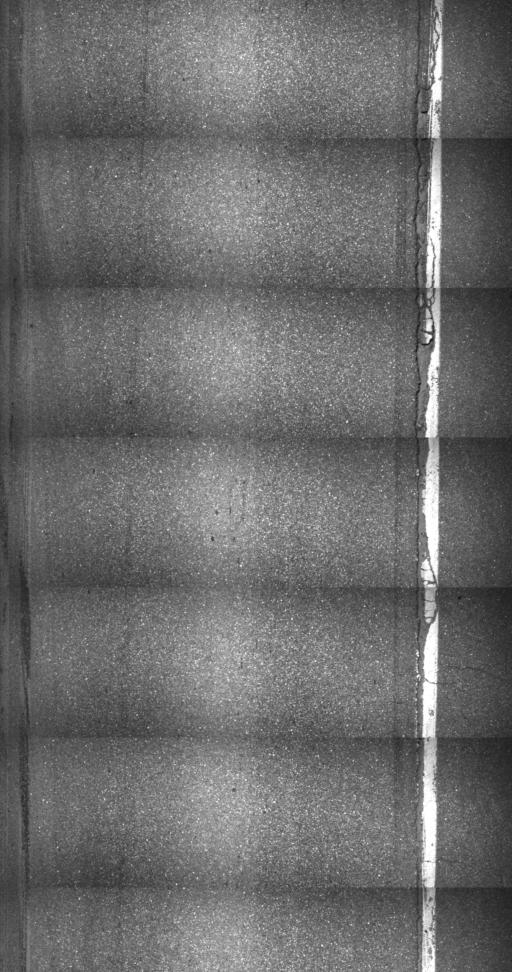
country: US
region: Vermont
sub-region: Chittenden County
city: Jericho
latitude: 44.6248
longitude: -72.9226
